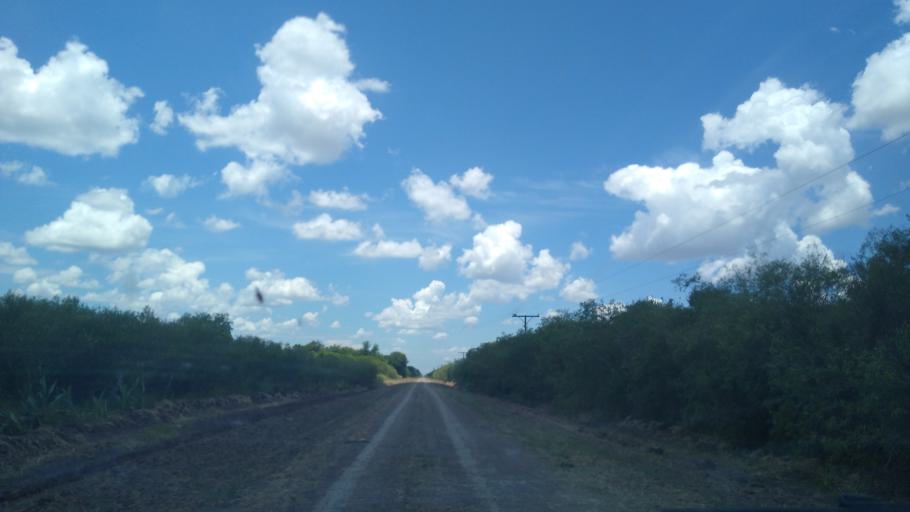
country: AR
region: Chaco
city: Presidencia Roque Saenz Pena
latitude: -26.7428
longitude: -60.3342
